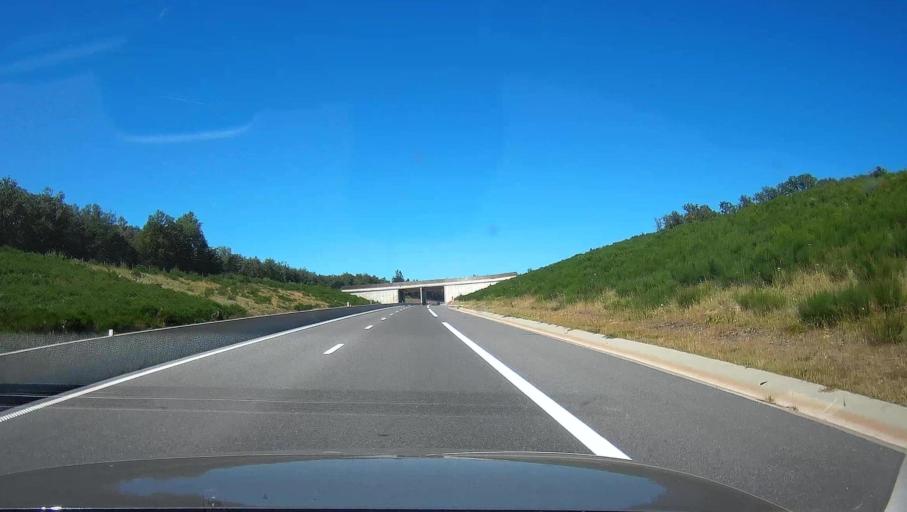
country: FR
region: Champagne-Ardenne
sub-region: Departement des Ardennes
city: Rimogne
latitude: 49.8615
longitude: 4.5106
